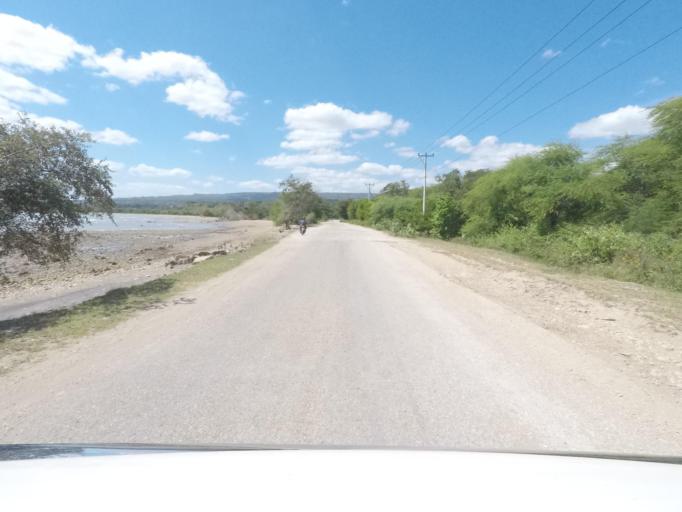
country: TL
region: Lautem
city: Lospalos
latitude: -8.3712
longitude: 126.8825
